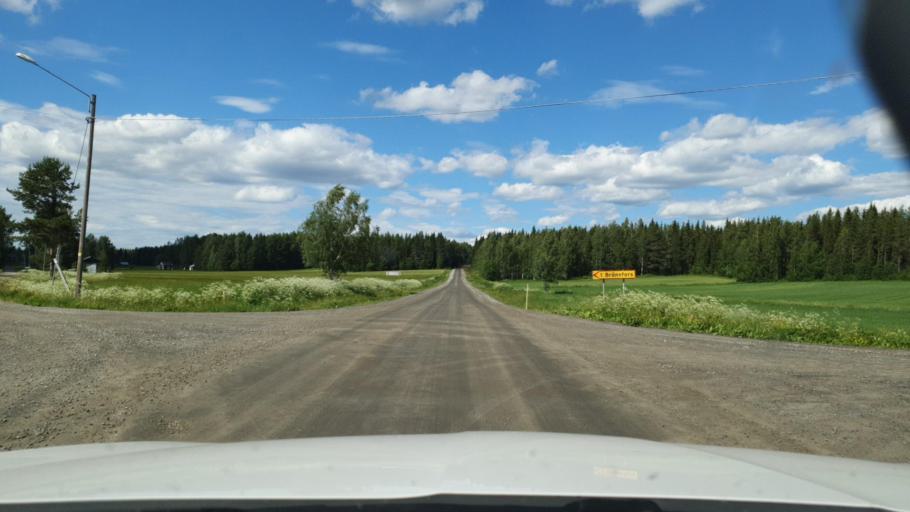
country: SE
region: Vaesterbotten
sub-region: Skelleftea Kommun
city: Forsbacka
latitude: 64.7896
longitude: 20.5100
